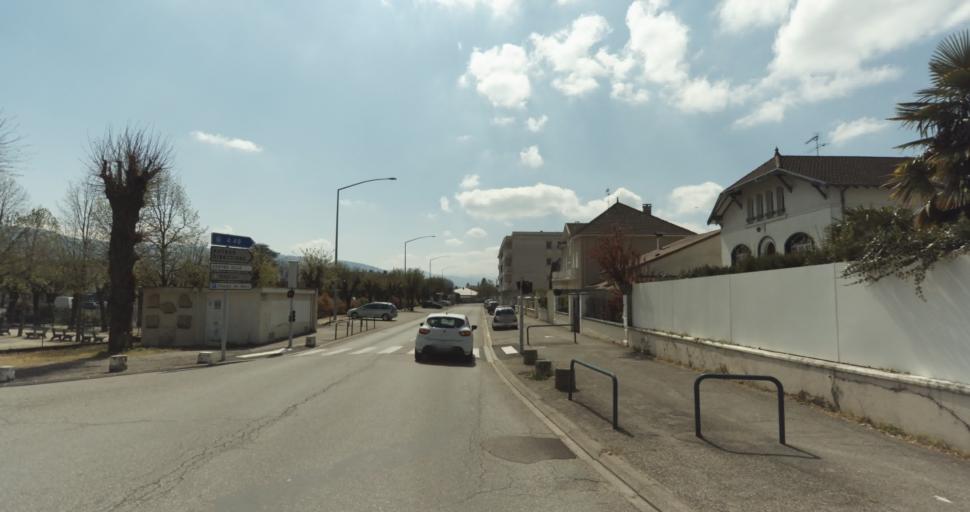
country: FR
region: Rhone-Alpes
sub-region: Departement de l'Isere
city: Saint-Marcellin
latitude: 45.1556
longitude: 5.3174
